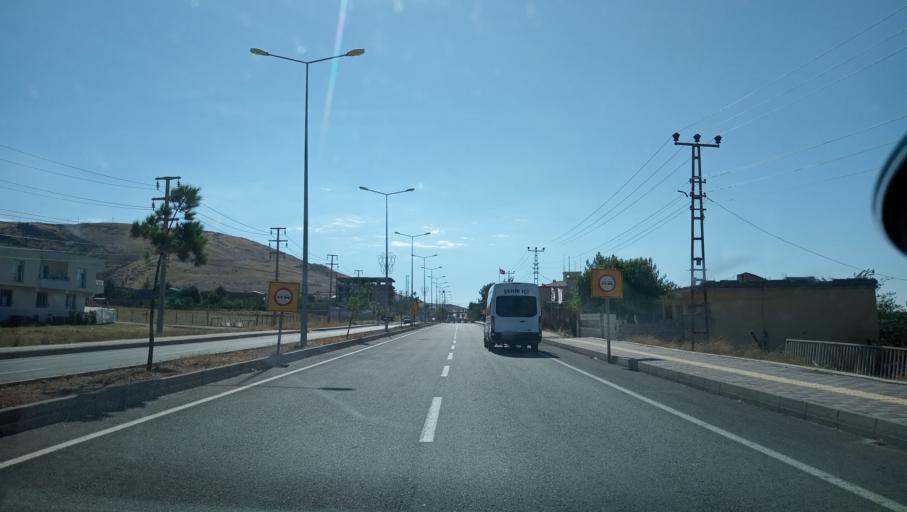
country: TR
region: Diyarbakir
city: Silvan
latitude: 38.1356
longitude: 41.0280
